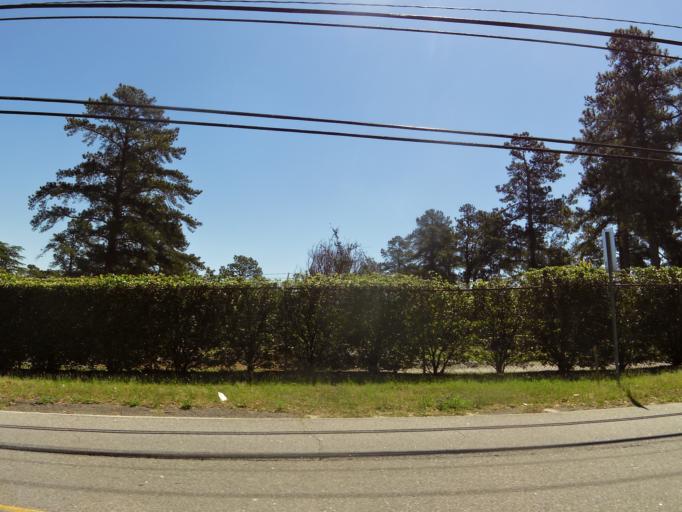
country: US
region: Georgia
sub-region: Columbia County
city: Martinez
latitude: 33.4861
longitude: -82.0297
